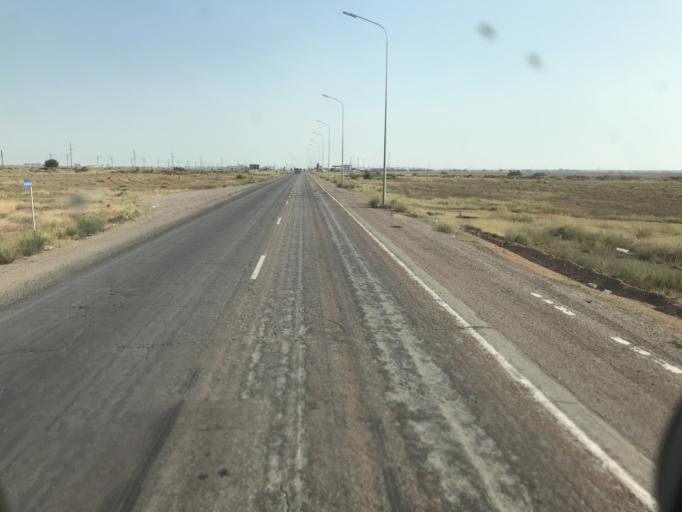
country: KZ
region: Qaraghandy
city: Balqash
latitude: 46.8843
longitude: 74.9488
